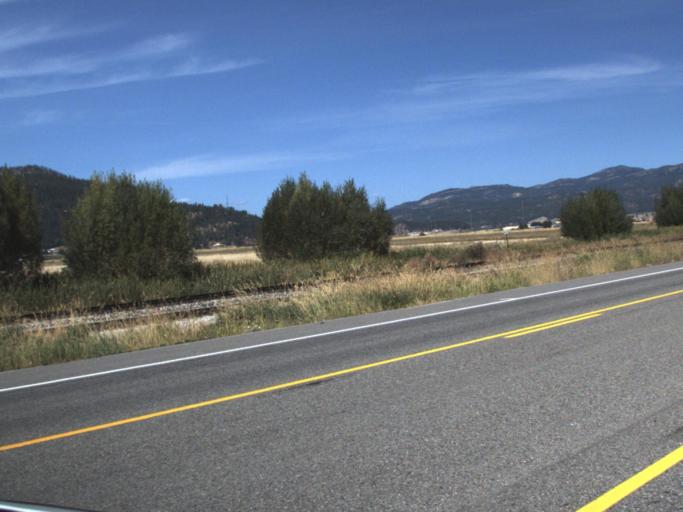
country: US
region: Washington
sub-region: Stevens County
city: Chewelah
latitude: 48.2427
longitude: -117.7152
